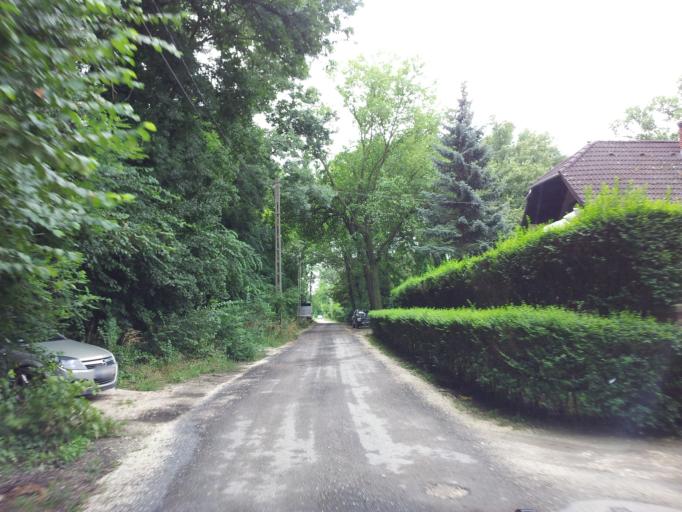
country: HU
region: Pest
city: Szigetujfalu
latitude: 47.2202
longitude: 18.9697
